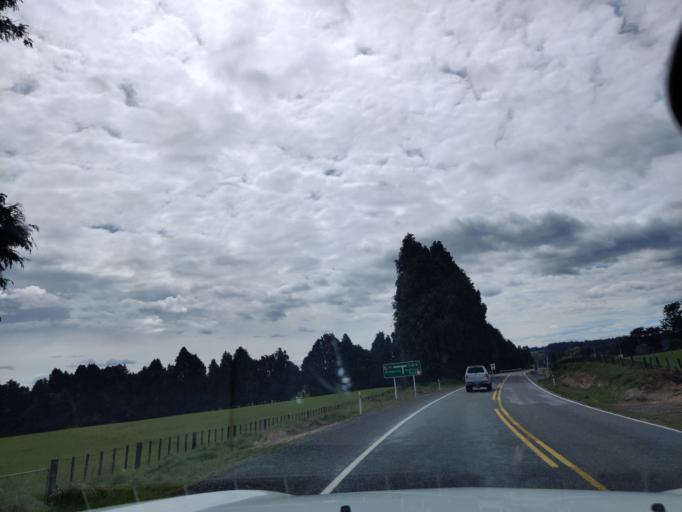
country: NZ
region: Manawatu-Wanganui
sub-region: Ruapehu District
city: Waiouru
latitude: -39.3697
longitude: 175.3229
